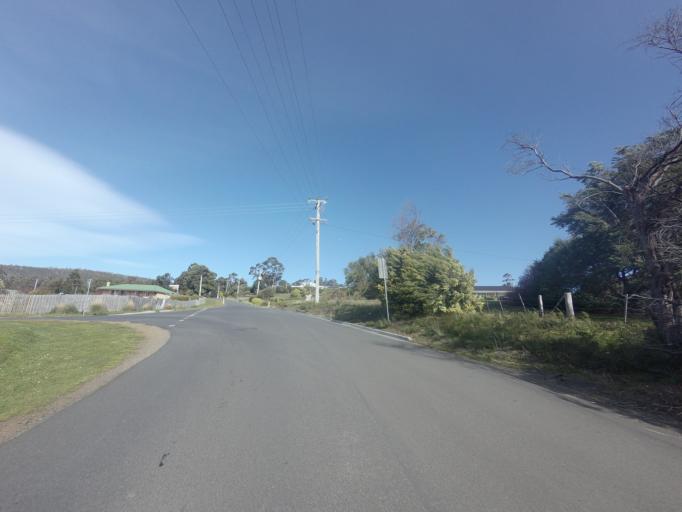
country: AU
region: Tasmania
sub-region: Kingborough
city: Margate
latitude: -43.0747
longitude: 147.2650
